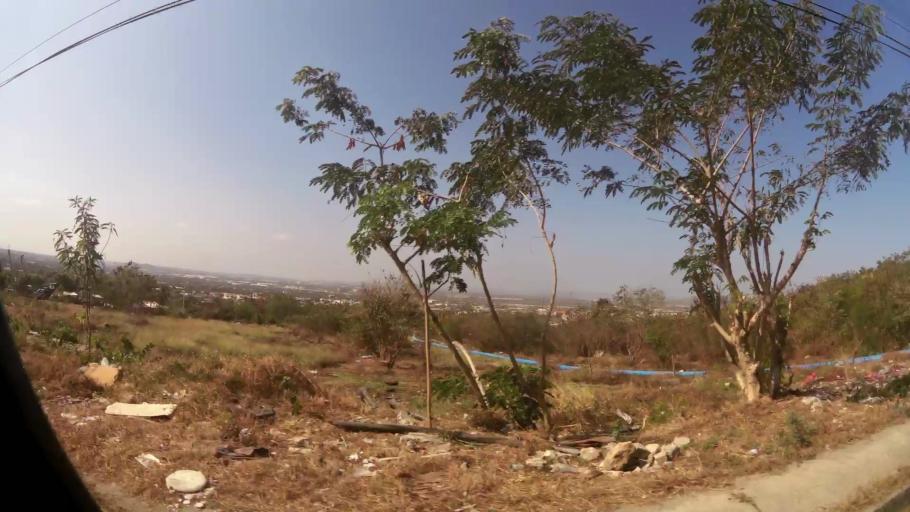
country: CO
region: Atlantico
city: Barranquilla
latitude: 10.9838
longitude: -74.8251
